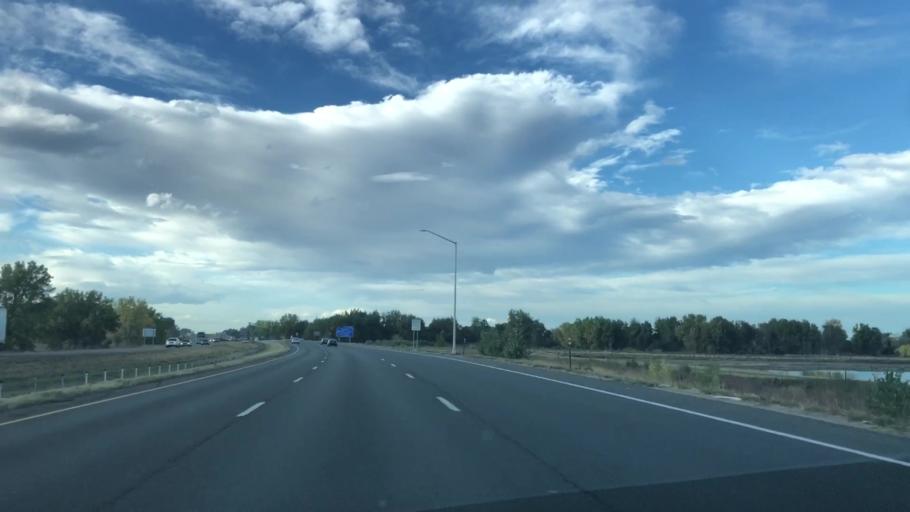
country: US
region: Colorado
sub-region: Weld County
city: Windsor
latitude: 40.5270
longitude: -104.9924
